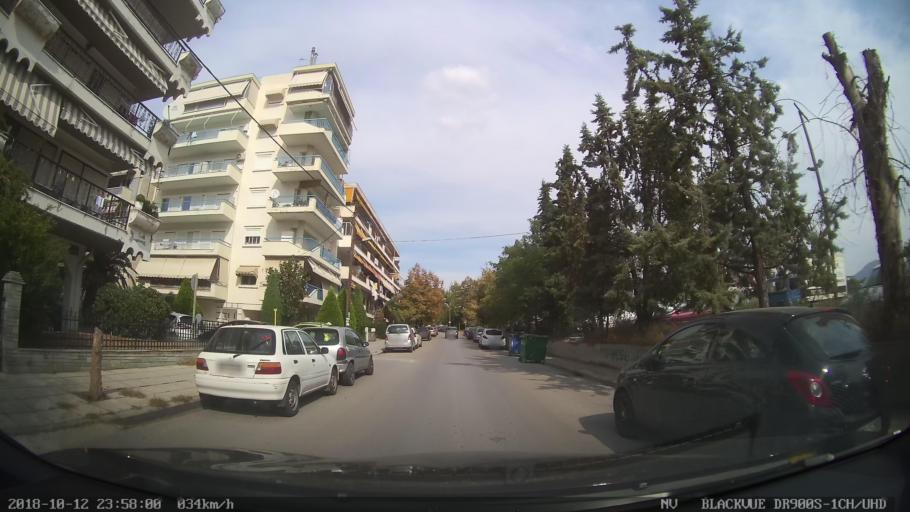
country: GR
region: Central Macedonia
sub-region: Nomos Thessalonikis
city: Pylaia
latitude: 40.6072
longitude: 22.9859
